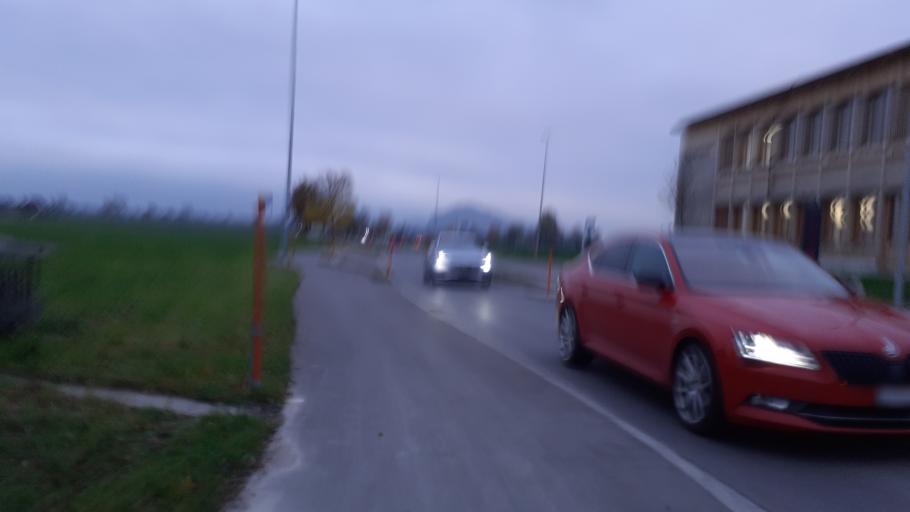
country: CH
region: Saint Gallen
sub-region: Wahlkreis Rheintal
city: Altstatten
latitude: 47.3738
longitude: 9.5625
